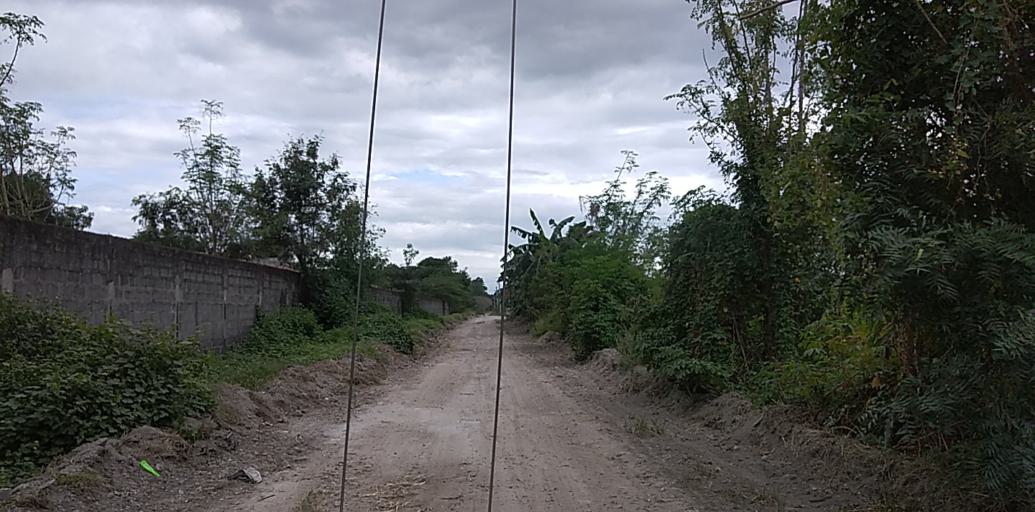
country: PH
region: Central Luzon
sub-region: Province of Pampanga
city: Pulung Santol
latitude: 15.0399
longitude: 120.5585
